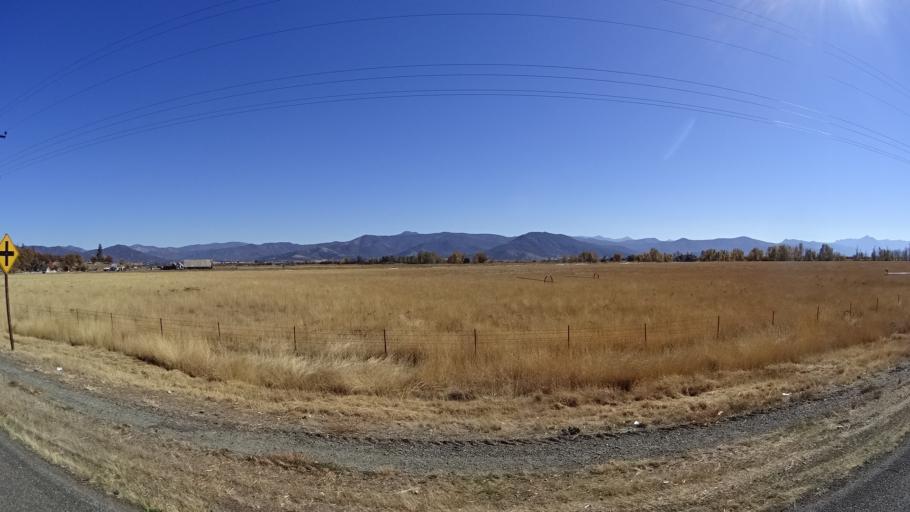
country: US
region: California
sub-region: Siskiyou County
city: Yreka
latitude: 41.5510
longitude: -122.9014
